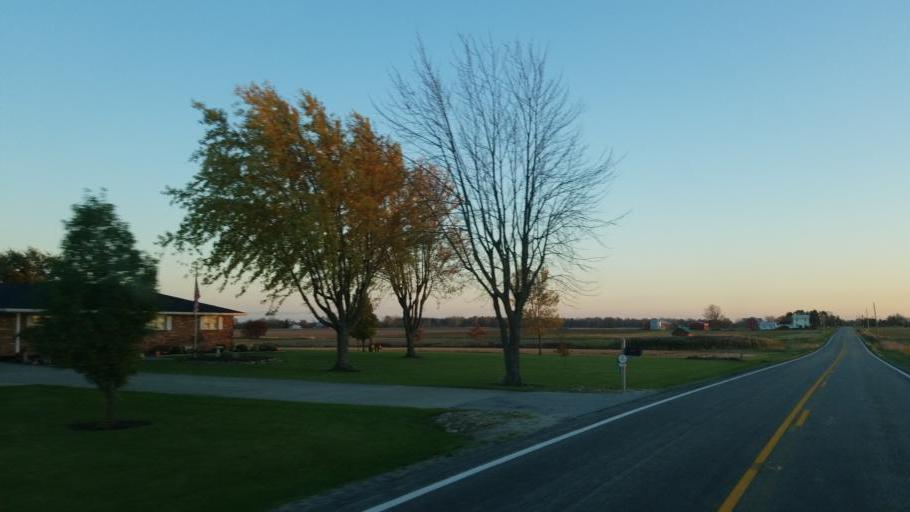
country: US
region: Ohio
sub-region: Huron County
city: Willard
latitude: 41.1221
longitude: -82.7854
